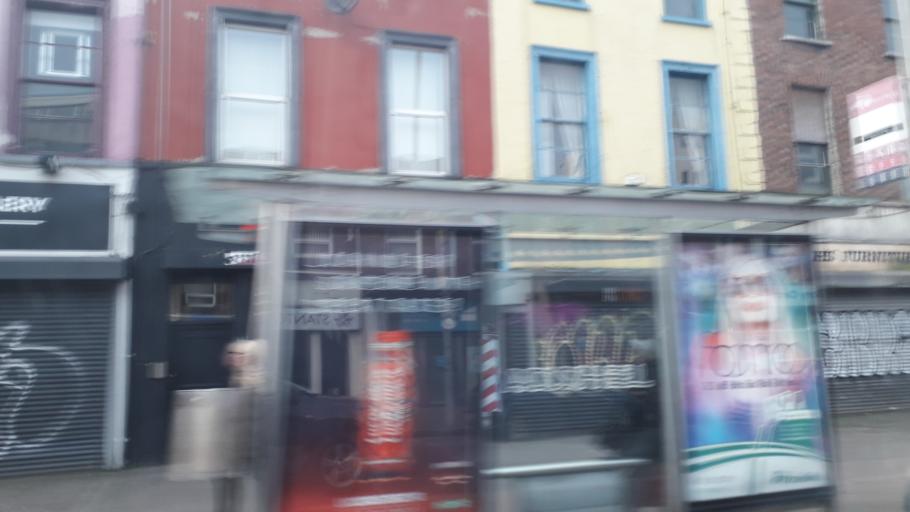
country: GB
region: Northern Ireland
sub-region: City of Belfast
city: Belfast
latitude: 54.5907
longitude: -5.9342
